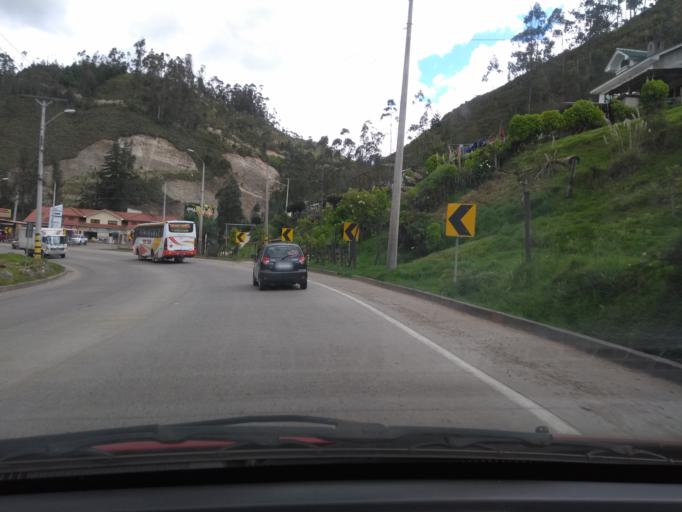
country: EC
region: Azuay
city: Cuenca
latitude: -2.9800
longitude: -79.0481
